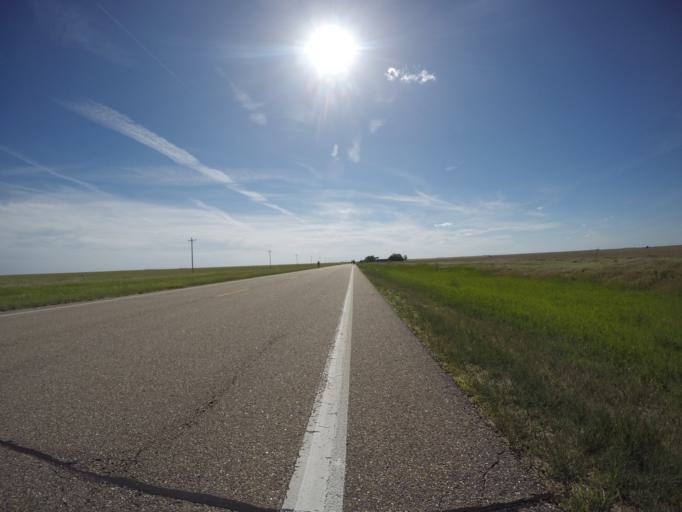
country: US
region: Kansas
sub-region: Cheyenne County
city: Saint Francis
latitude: 39.7566
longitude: -101.9876
